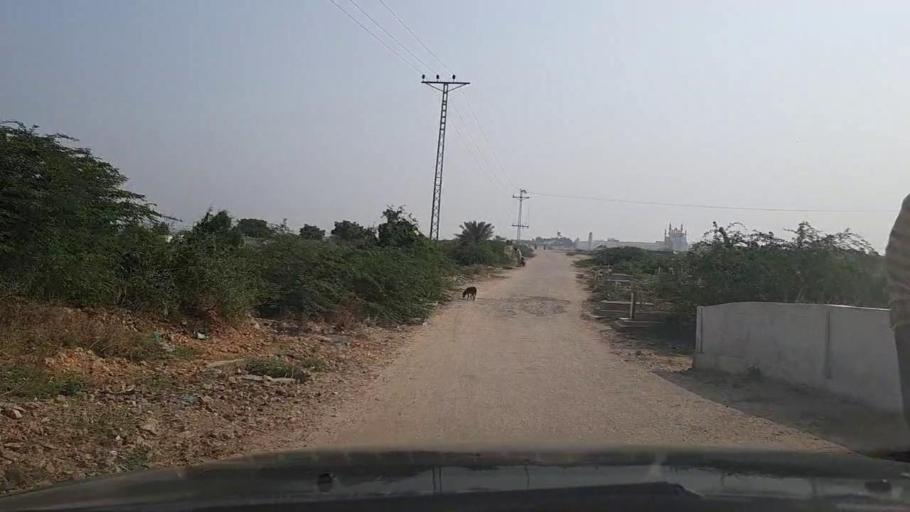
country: PK
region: Sindh
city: Thatta
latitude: 24.7452
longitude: 67.8995
